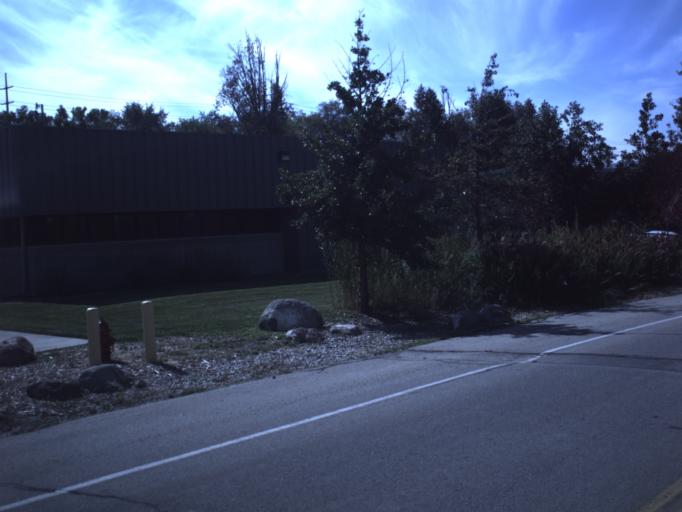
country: US
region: Utah
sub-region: Salt Lake County
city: Bluffdale
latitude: 40.4884
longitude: -111.8978
